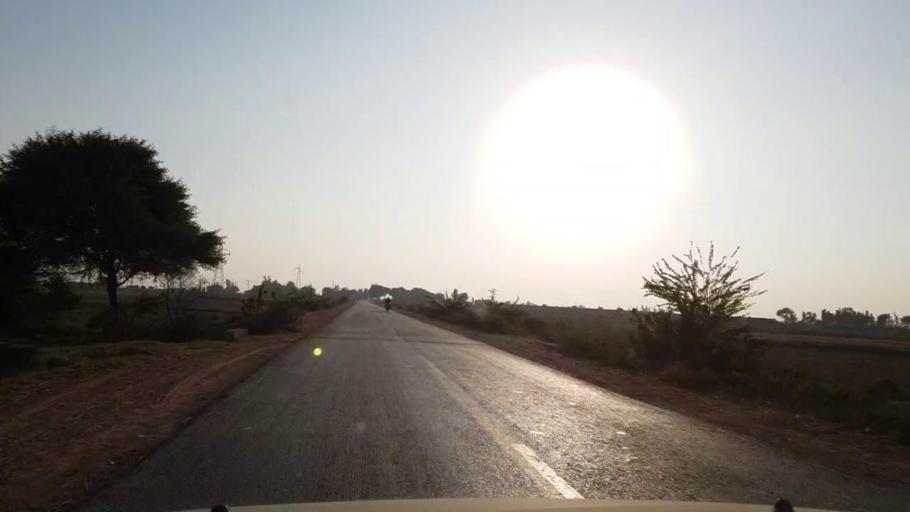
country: PK
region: Sindh
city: Daro Mehar
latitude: 24.6442
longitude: 68.1204
